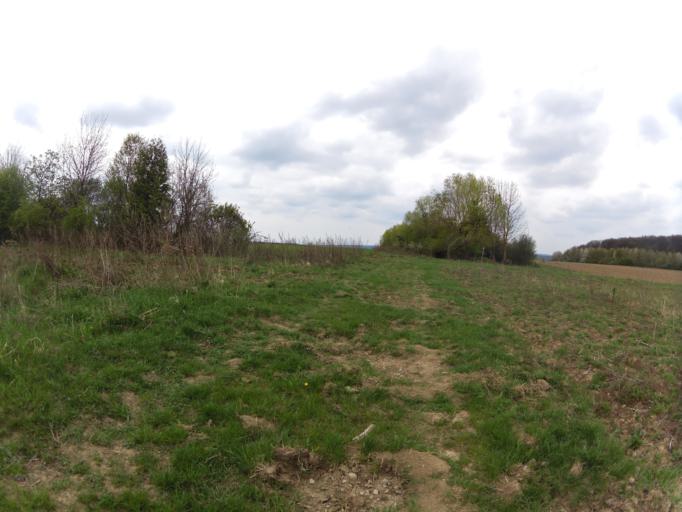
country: DE
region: Bavaria
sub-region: Regierungsbezirk Unterfranken
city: Greussenheim
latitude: 49.8285
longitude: 9.7966
